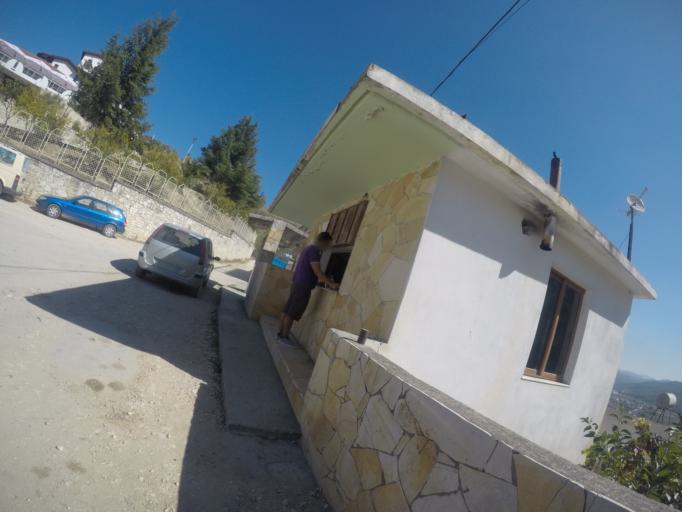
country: AL
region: Berat
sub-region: Rrethi i Beratit
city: Berat
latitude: 40.7113
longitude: 19.9469
